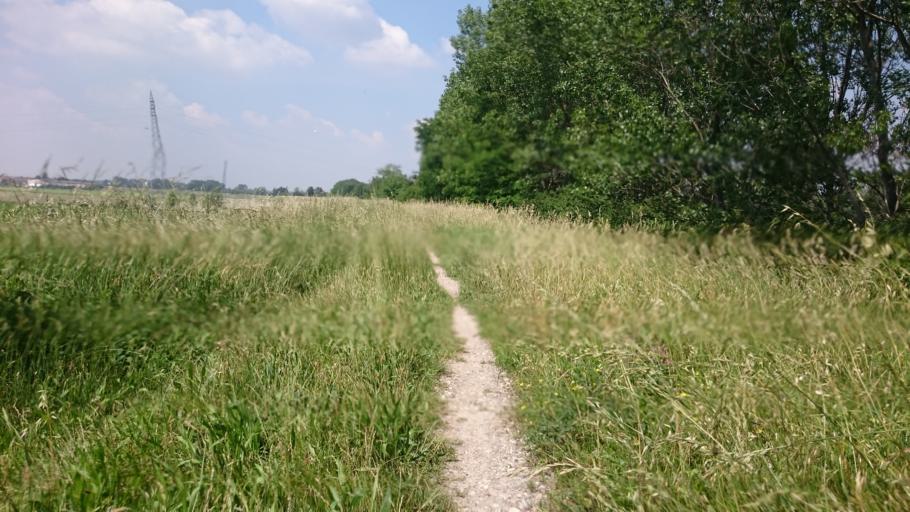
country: IT
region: Lombardy
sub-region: Provincia di Mantova
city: San Biagio
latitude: 45.1221
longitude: 10.8523
